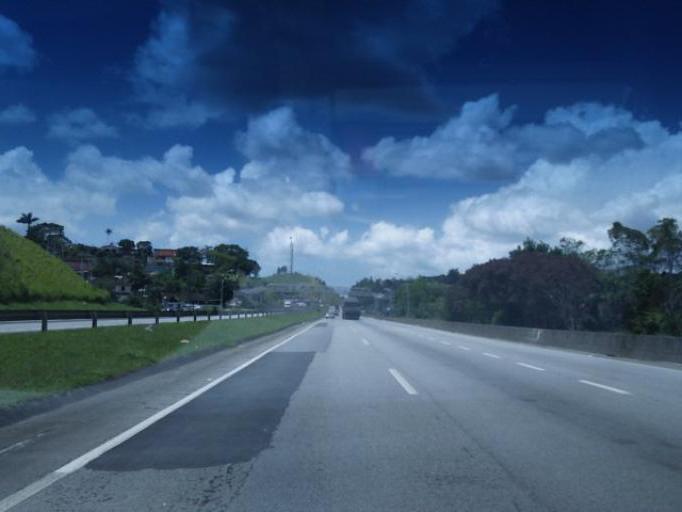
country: BR
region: Sao Paulo
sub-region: Juquitiba
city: Juquitiba
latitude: -23.9779
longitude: -47.1445
